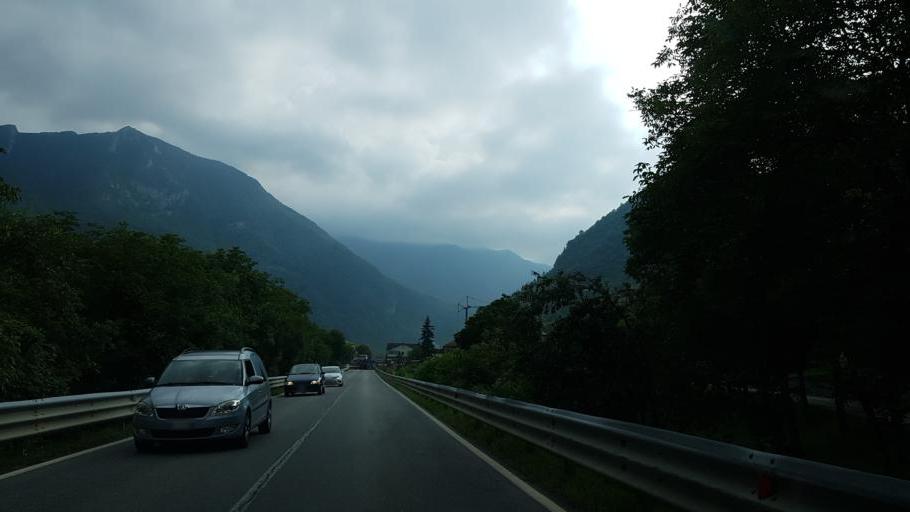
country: IT
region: Piedmont
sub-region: Provincia di Cuneo
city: Moiola
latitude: 44.3222
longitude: 7.3919
